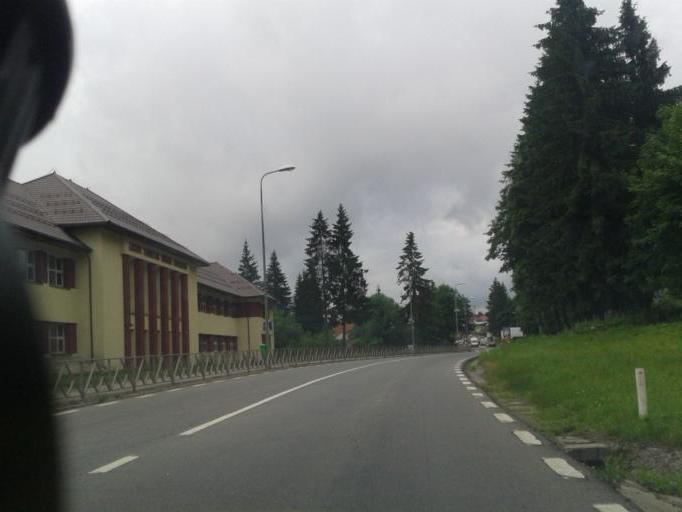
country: RO
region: Brasov
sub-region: Oras Predeal
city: Predeal
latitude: 45.4969
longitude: 25.5721
